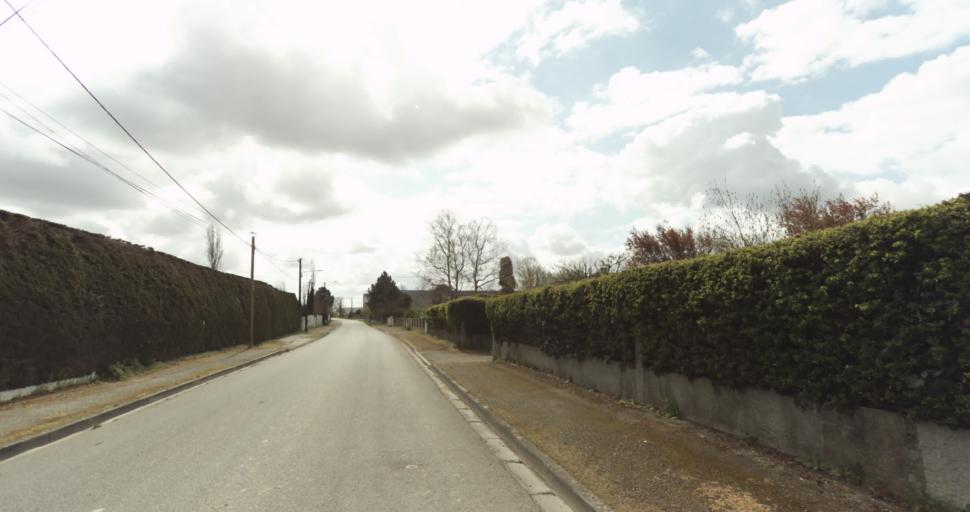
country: FR
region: Midi-Pyrenees
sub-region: Departement de la Haute-Garonne
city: Auterive
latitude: 43.3668
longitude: 1.4615
